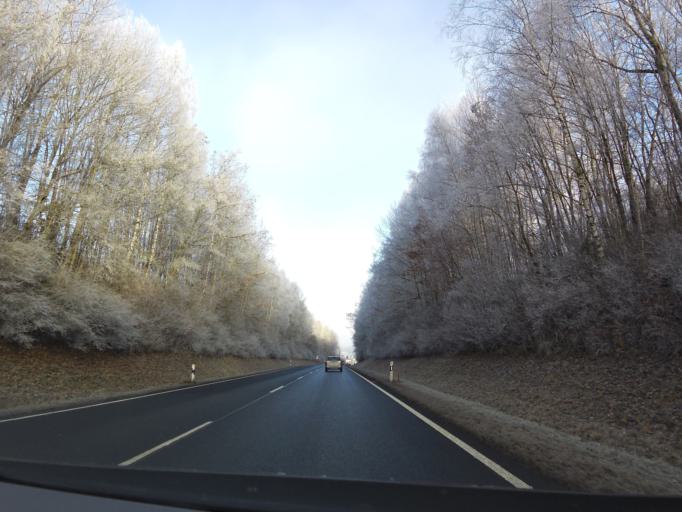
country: DE
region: Bavaria
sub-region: Upper Franconia
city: Arzberg
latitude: 50.0514
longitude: 12.1692
